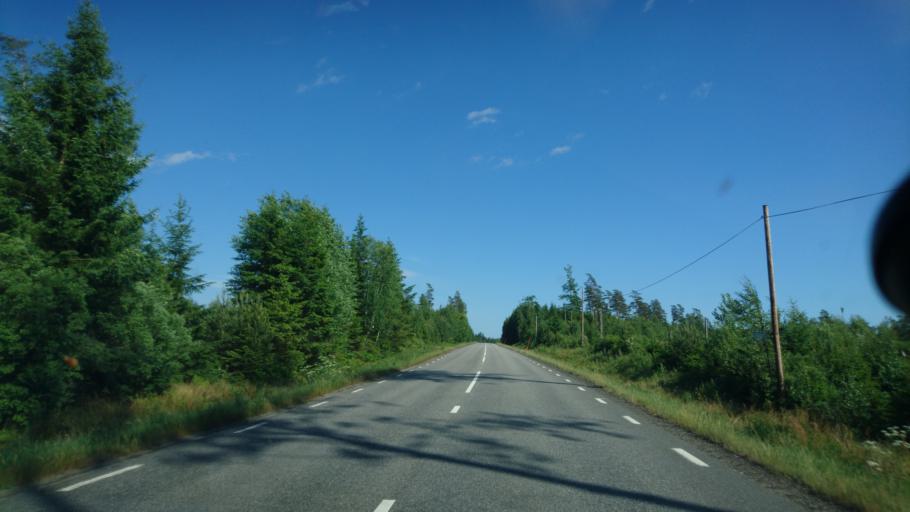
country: SE
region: Skane
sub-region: Osby Kommun
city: Lonsboda
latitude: 56.4269
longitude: 14.2735
